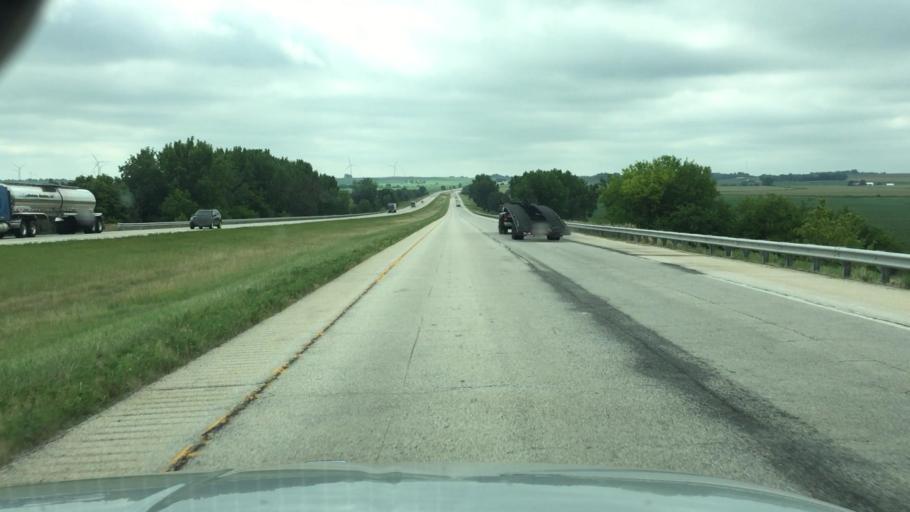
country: US
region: Illinois
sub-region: Henry County
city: Orion
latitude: 41.2784
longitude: -90.3337
